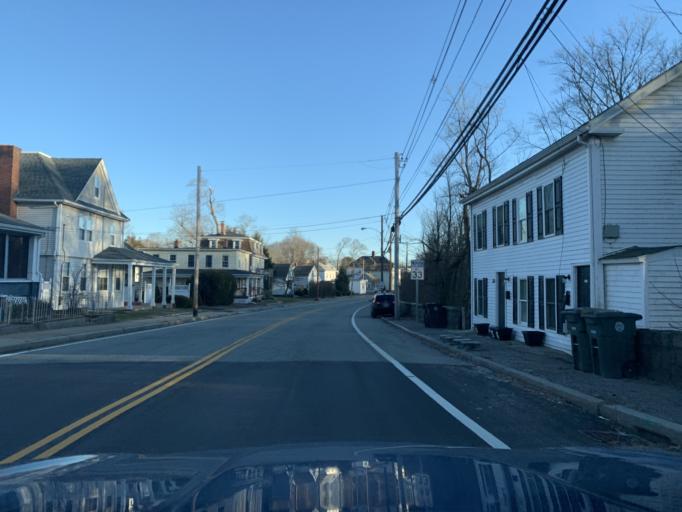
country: US
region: Rhode Island
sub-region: Kent County
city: West Warwick
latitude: 41.6972
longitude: -71.5433
